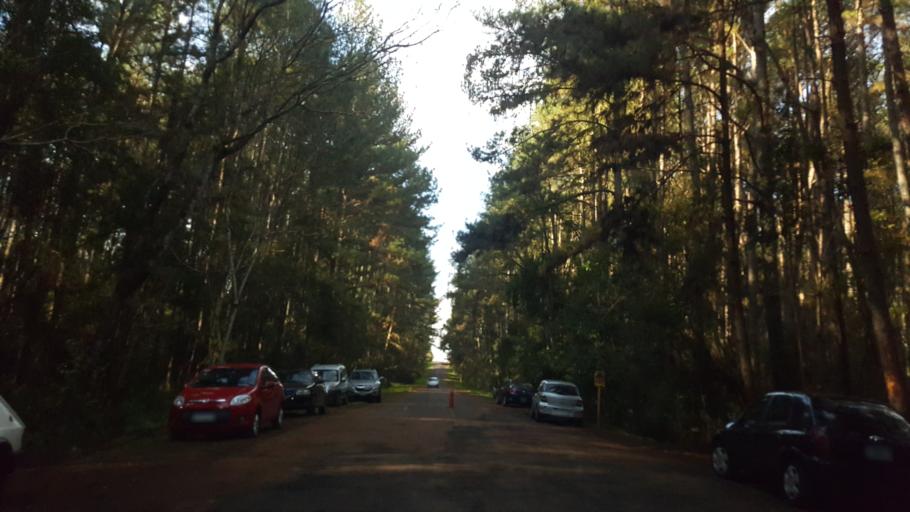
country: AR
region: Misiones
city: Puerto Leoni
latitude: -27.0048
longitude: -55.1884
